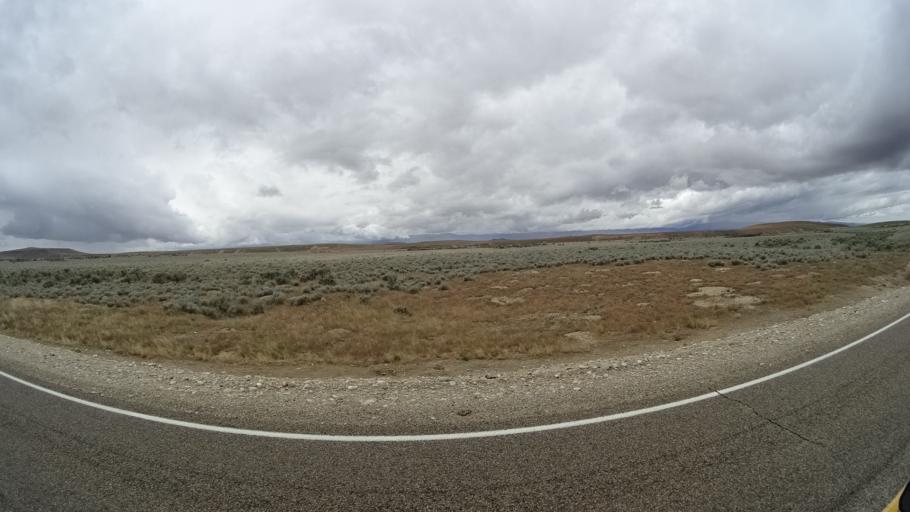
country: US
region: Idaho
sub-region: Owyhee County
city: Murphy
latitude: 43.2739
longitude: -116.3917
